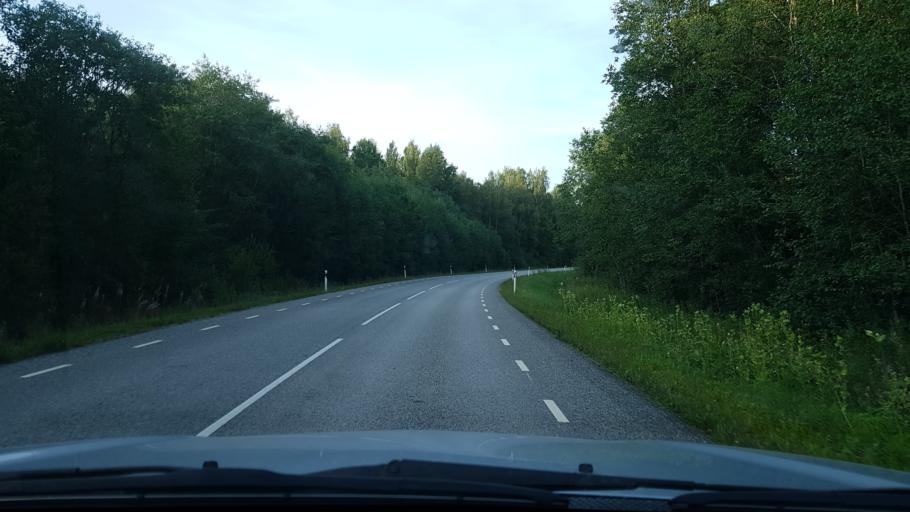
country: EE
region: Ida-Virumaa
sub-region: Sillamaee linn
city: Sillamae
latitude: 59.3288
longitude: 27.9204
